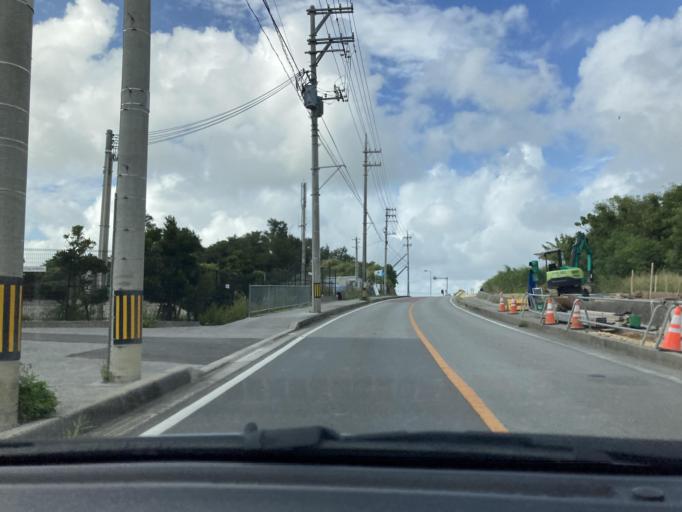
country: JP
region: Okinawa
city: Itoman
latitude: 26.1085
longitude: 127.6943
